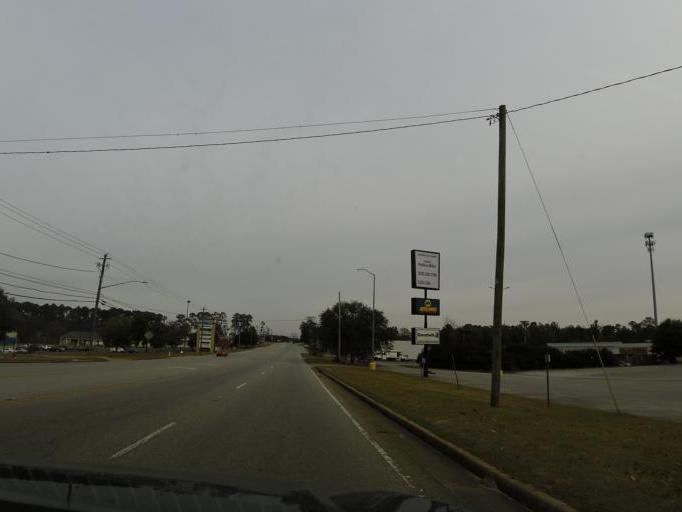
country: US
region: Georgia
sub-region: Decatur County
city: Bainbridge
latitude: 30.9038
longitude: -84.5507
